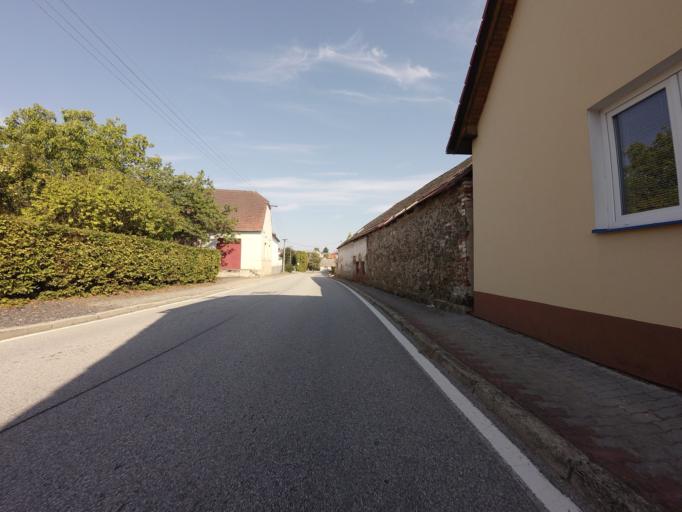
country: CZ
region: Jihocesky
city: Bernartice
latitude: 49.2940
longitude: 14.3891
